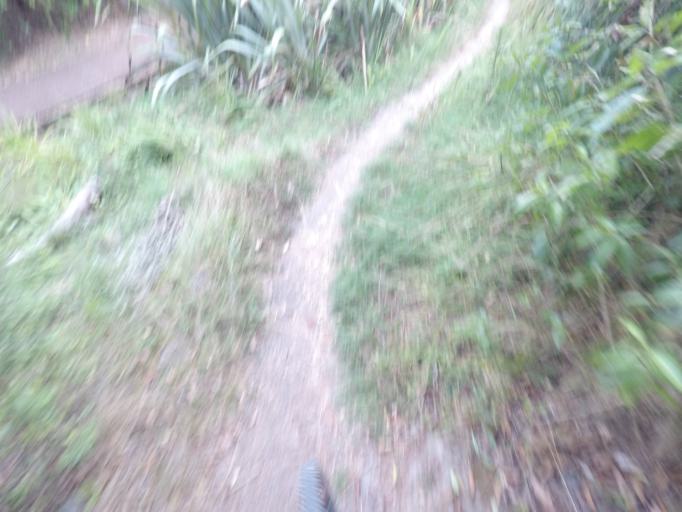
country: NZ
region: Auckland
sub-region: Auckland
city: Auckland
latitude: -36.8680
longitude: 174.7385
